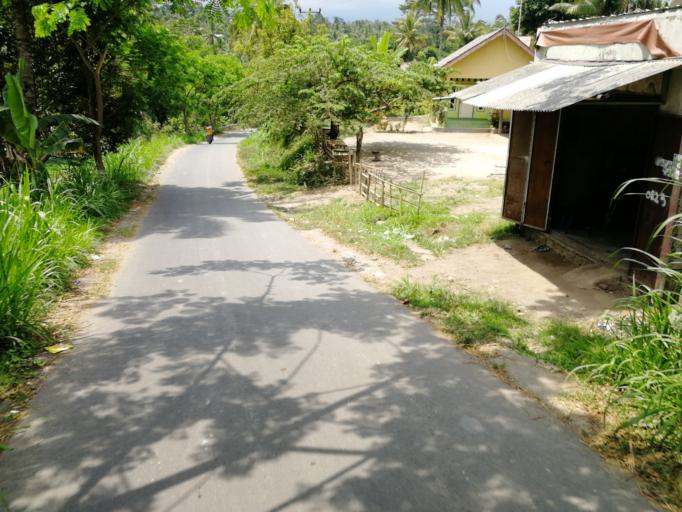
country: ID
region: West Nusa Tenggara
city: Pediti
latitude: -8.5597
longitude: 116.3325
